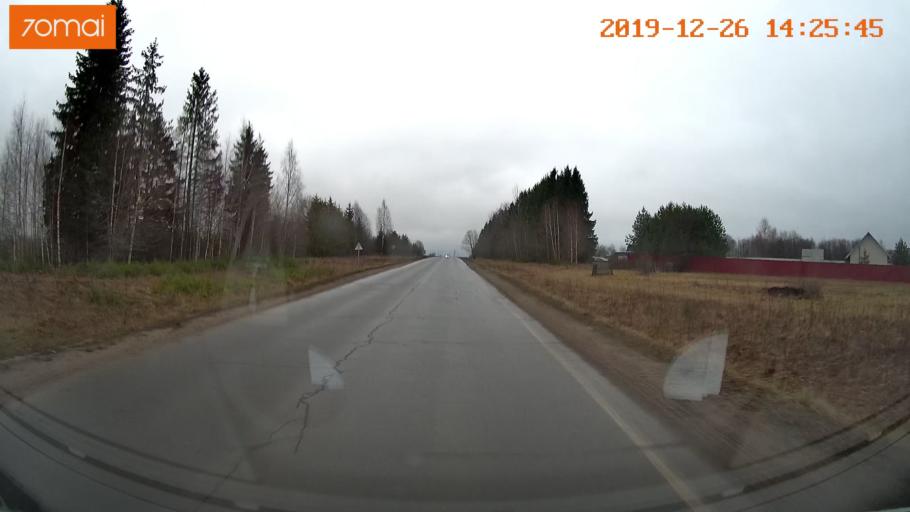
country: RU
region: Jaroslavl
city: Poshekhon'ye
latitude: 58.4921
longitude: 39.0904
